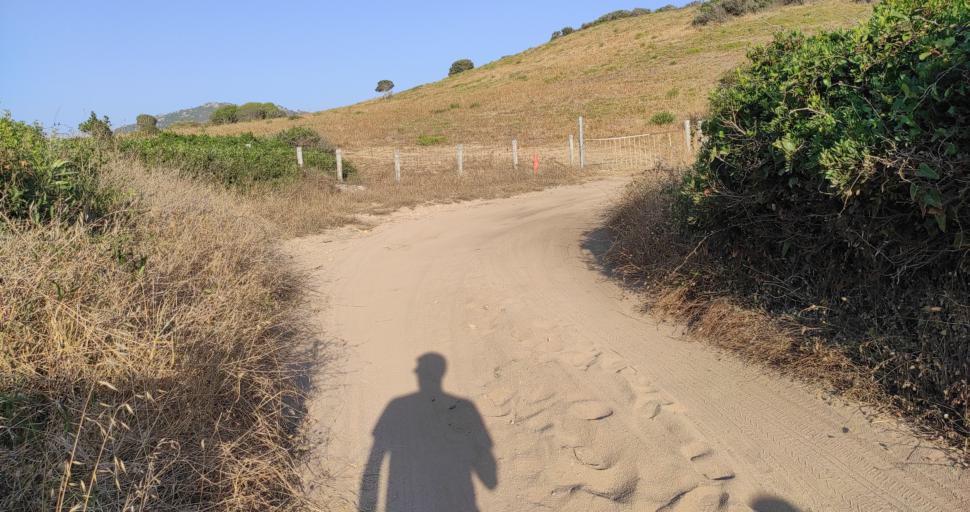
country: FR
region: Corsica
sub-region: Departement de la Corse-du-Sud
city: Alata
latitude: 41.9878
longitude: 8.6712
